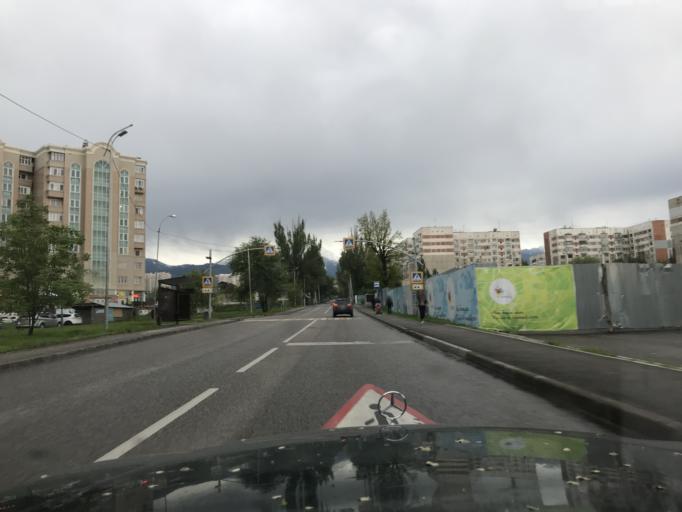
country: KZ
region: Almaty Qalasy
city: Almaty
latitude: 43.2161
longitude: 76.8813
